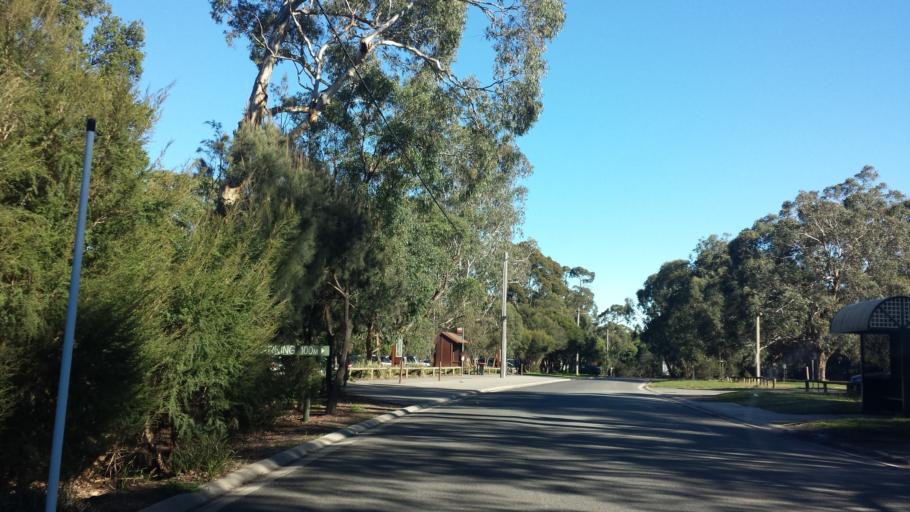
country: AU
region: Victoria
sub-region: Yarra Ranges
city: Badger Creek
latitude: -37.6816
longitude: 145.5316
